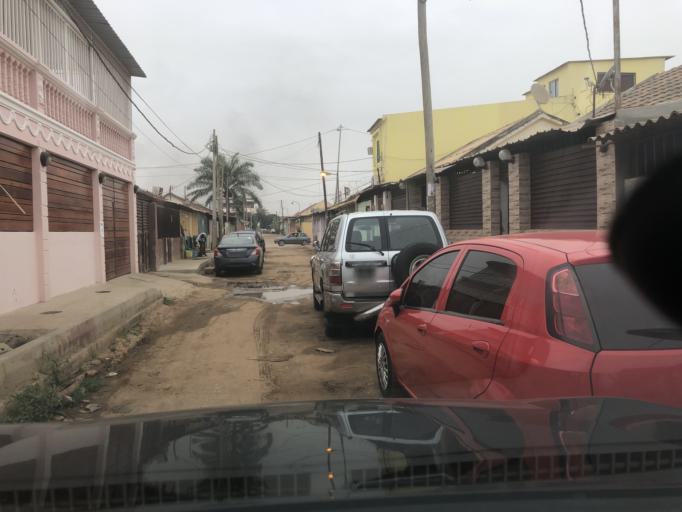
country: AO
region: Luanda
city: Luanda
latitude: -8.8460
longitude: 13.2598
